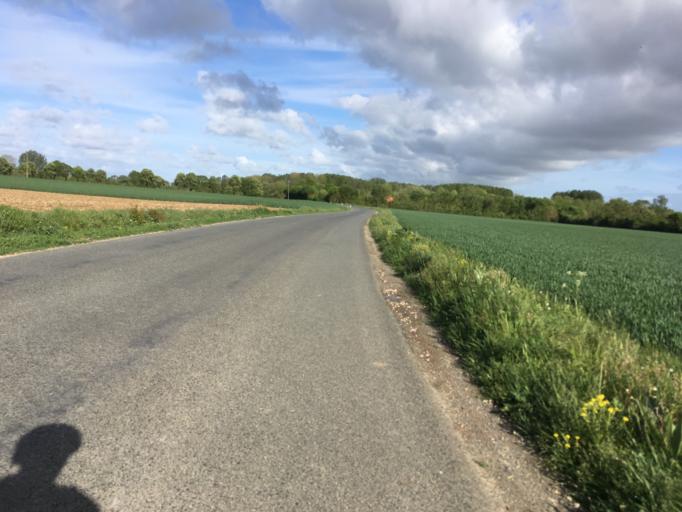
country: FR
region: Poitou-Charentes
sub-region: Departement de la Charente-Maritime
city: Verines
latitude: 46.1787
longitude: -0.9300
